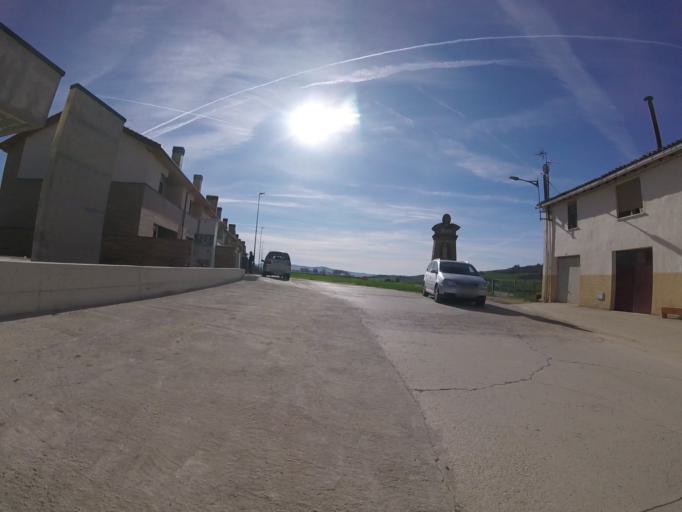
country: ES
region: Navarre
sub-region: Provincia de Navarra
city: Estella
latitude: 42.7240
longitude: -2.0211
